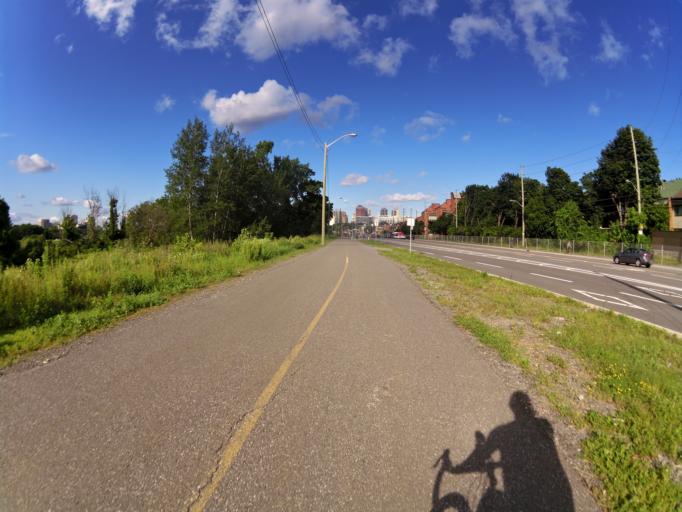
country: CA
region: Ontario
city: Ottawa
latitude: 45.4107
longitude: -75.7183
